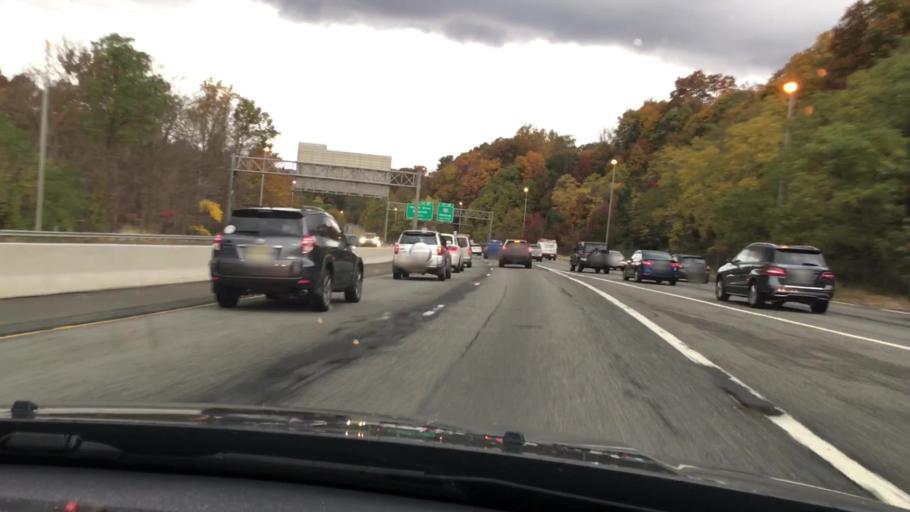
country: US
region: New Jersey
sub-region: Bergen County
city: Franklin Lakes
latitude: 41.0247
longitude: -74.2264
